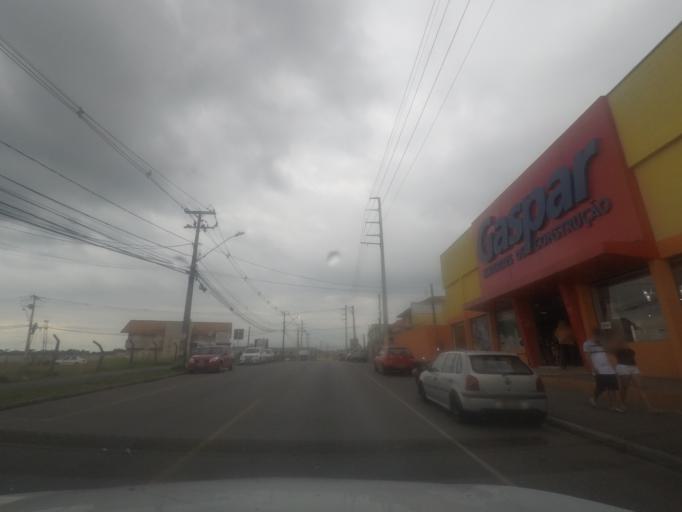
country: BR
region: Parana
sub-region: Sao Jose Dos Pinhais
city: Sao Jose dos Pinhais
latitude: -25.5562
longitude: -49.2538
